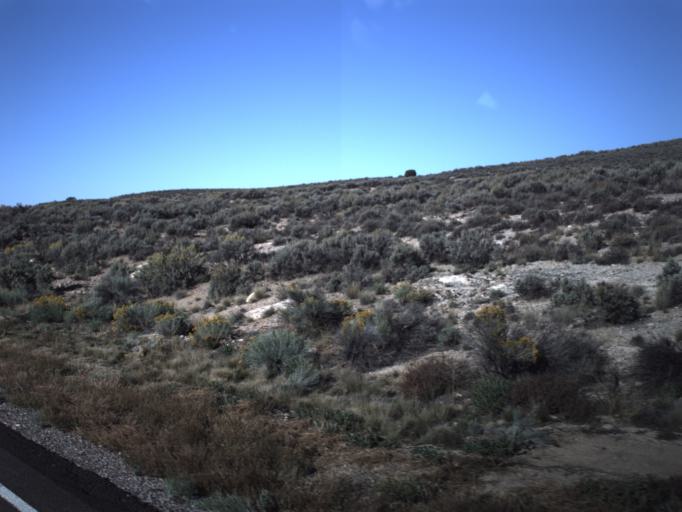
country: US
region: Utah
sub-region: Washington County
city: Enterprise
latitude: 37.7523
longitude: -113.9988
